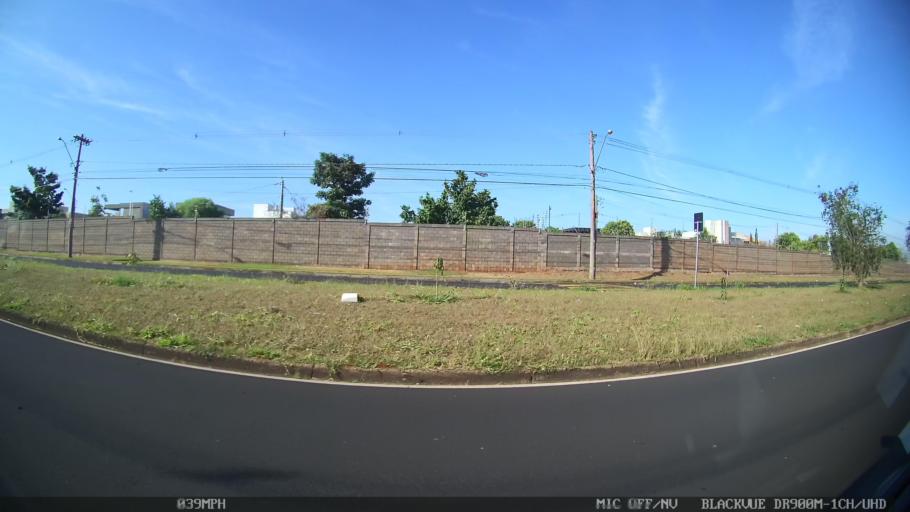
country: BR
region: Sao Paulo
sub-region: Sao Jose Do Rio Preto
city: Sao Jose do Rio Preto
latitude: -20.7763
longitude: -49.3404
